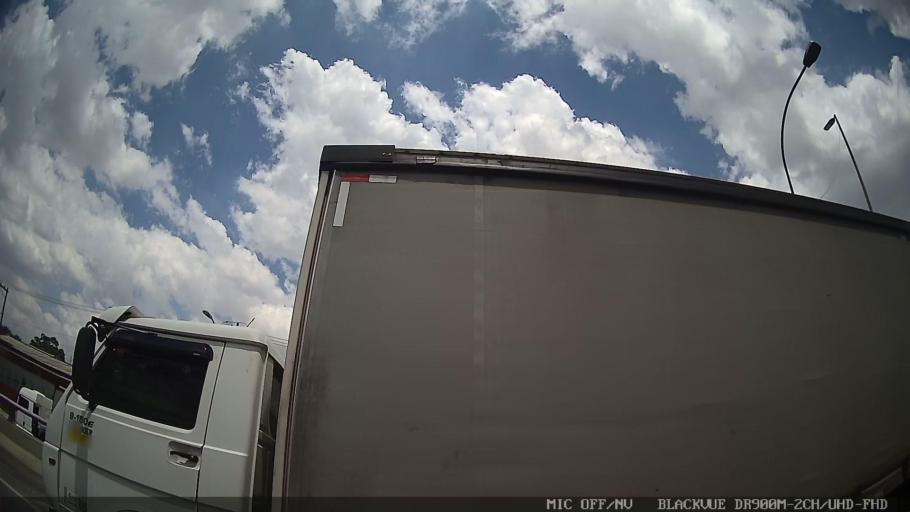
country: BR
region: Sao Paulo
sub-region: Osasco
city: Osasco
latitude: -23.5058
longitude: -46.7189
